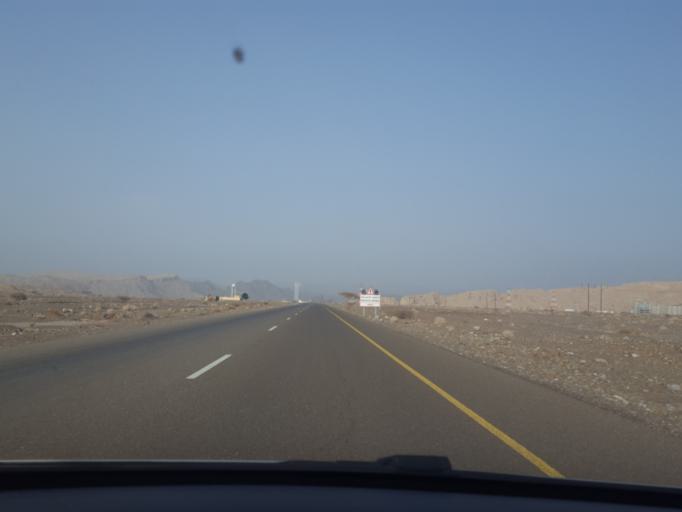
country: AE
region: Abu Dhabi
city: Al Ain
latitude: 24.0338
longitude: 56.0042
